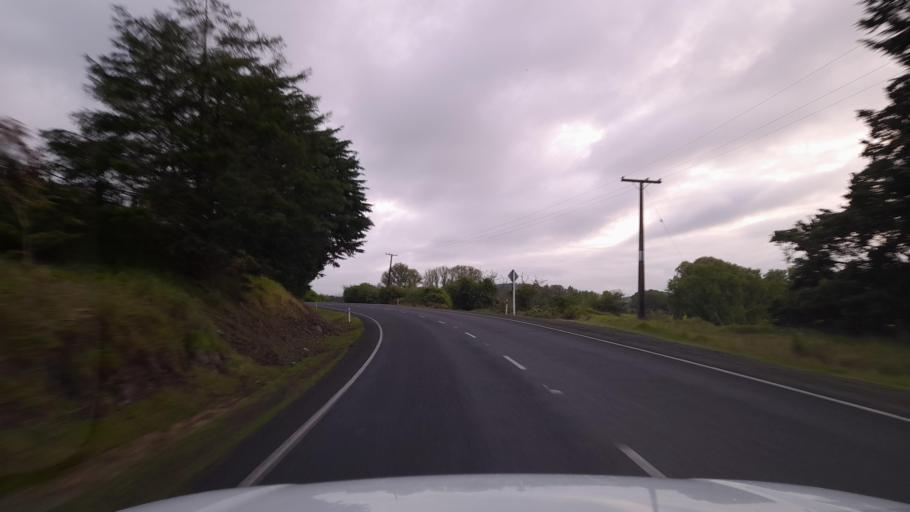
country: NZ
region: Northland
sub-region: Whangarei
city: Maungatapere
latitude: -35.7158
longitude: 174.0299
